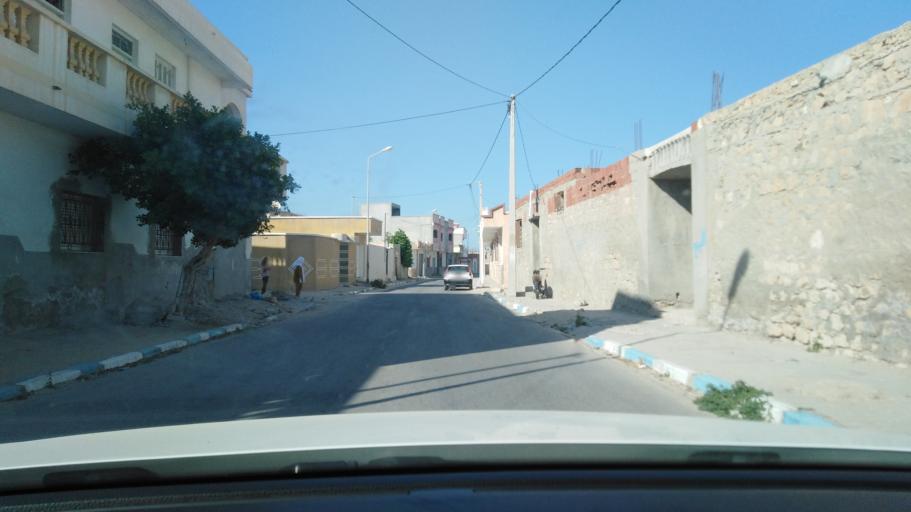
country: TN
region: Qabis
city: Gabes
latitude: 33.9392
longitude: 10.0694
